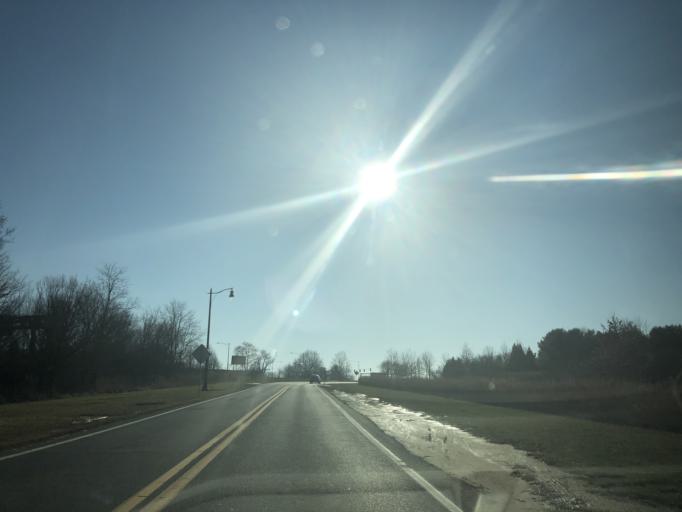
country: US
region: Delaware
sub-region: New Castle County
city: Wilmington
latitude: 39.7740
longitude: -75.5457
